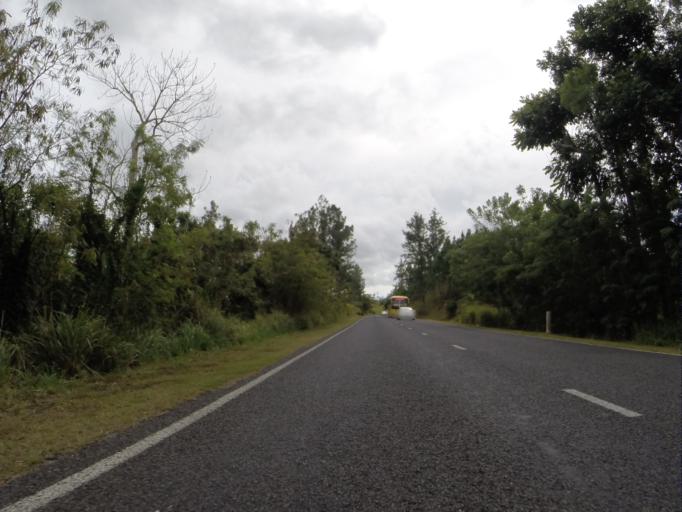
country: FJ
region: Western
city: Nadi
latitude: -17.9987
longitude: 177.3196
